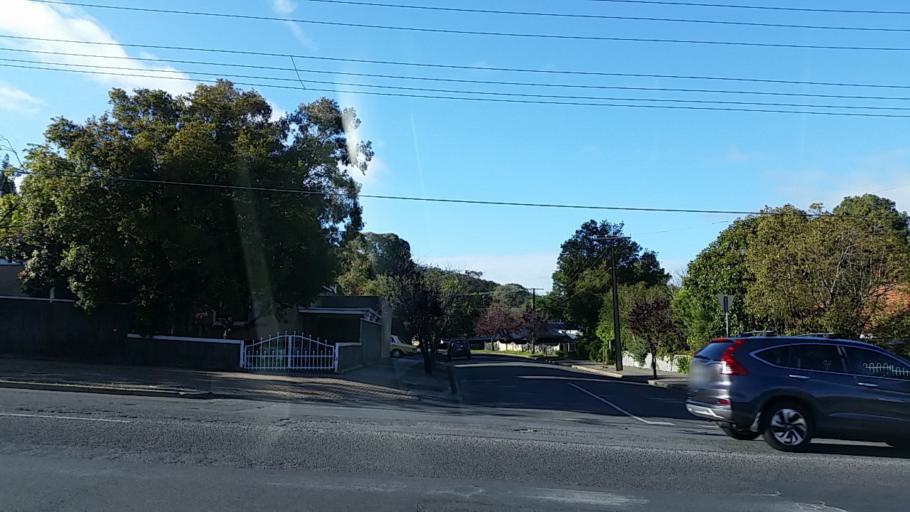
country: AU
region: South Australia
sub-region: Mitcham
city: Clapham
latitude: -34.9902
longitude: 138.6038
